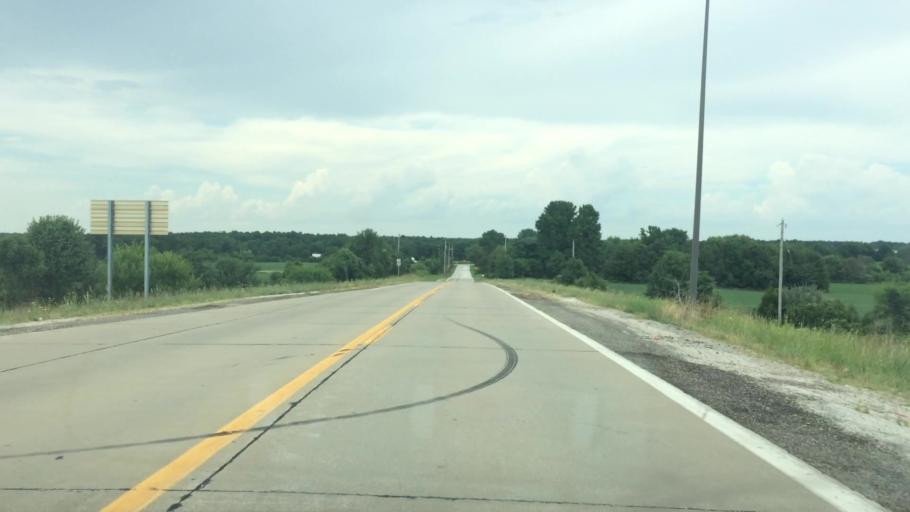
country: US
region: Missouri
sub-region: Greene County
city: Strafford
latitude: 37.2515
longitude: -93.1833
